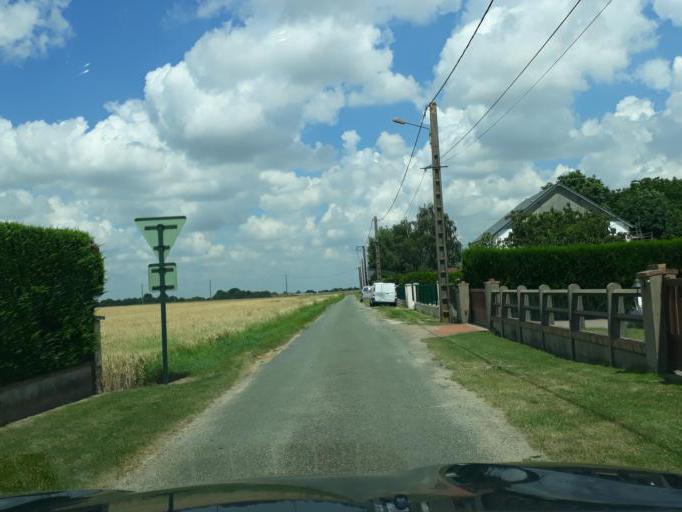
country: FR
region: Centre
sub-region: Departement du Loiret
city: Chevilly
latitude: 48.0379
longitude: 1.9086
